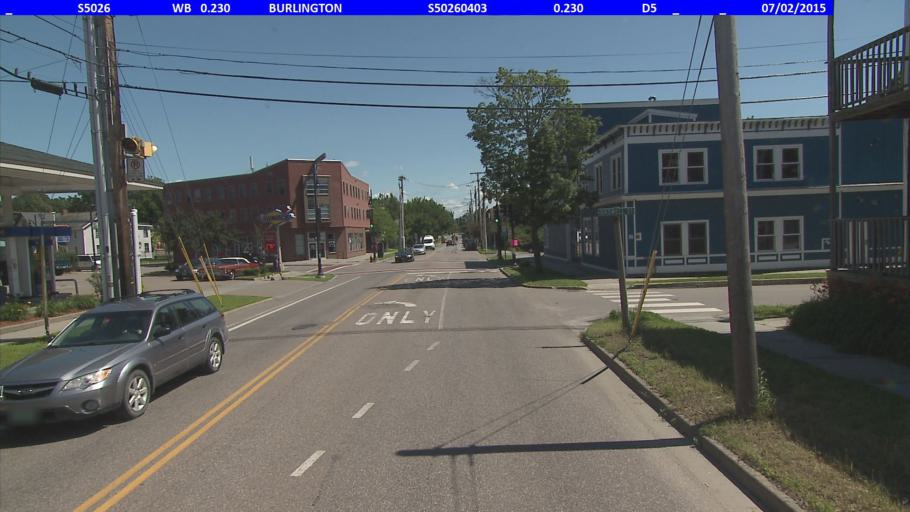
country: US
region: Vermont
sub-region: Chittenden County
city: Burlington
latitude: 44.4848
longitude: -73.2226
